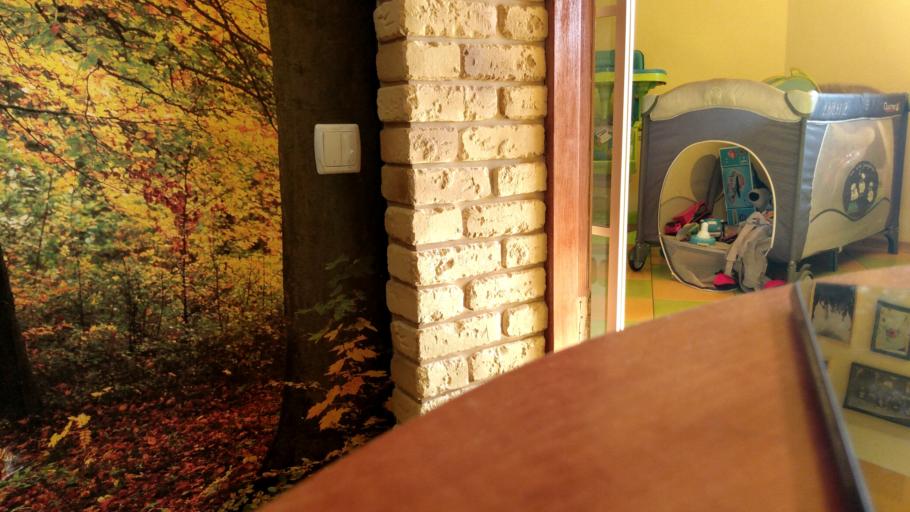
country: RU
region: Tverskaya
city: Radchenko
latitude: 56.6917
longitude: 36.4355
